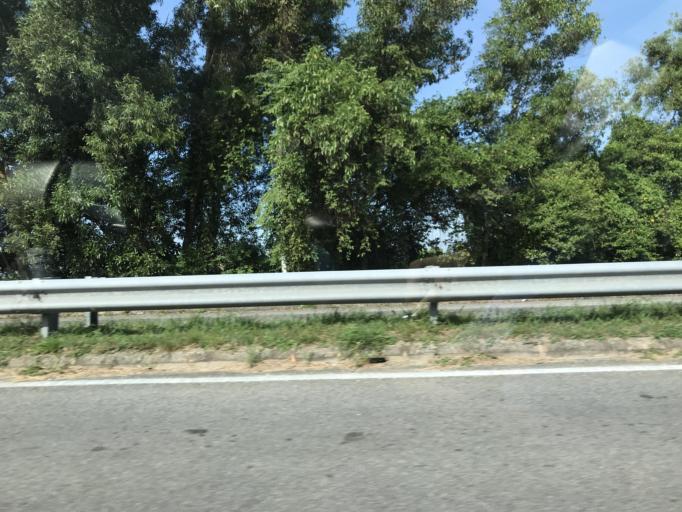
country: MY
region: Kelantan
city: Kampong Kadok
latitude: 6.0524
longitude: 102.2168
